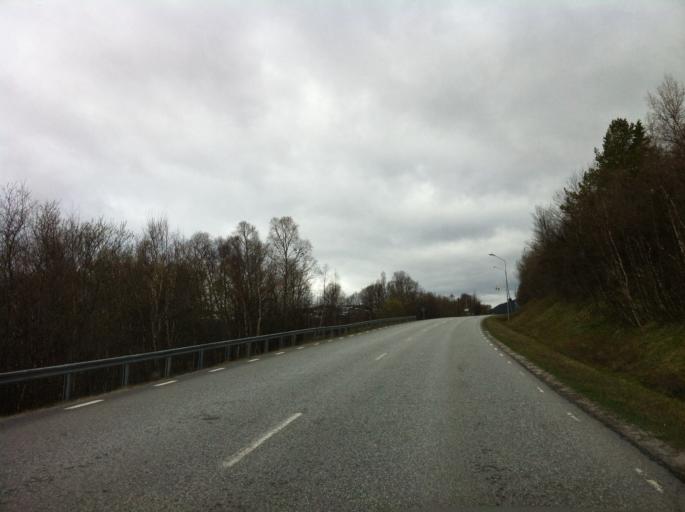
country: NO
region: Hedmark
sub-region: Engerdal
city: Engerdal
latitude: 62.5346
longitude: 12.3653
